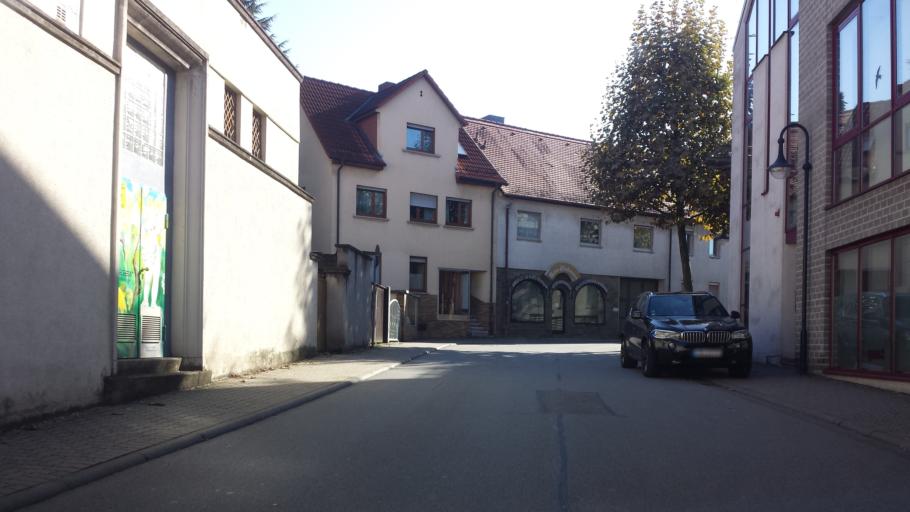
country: DE
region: Hesse
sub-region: Regierungsbezirk Darmstadt
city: Bensheim
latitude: 49.6803
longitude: 8.6235
